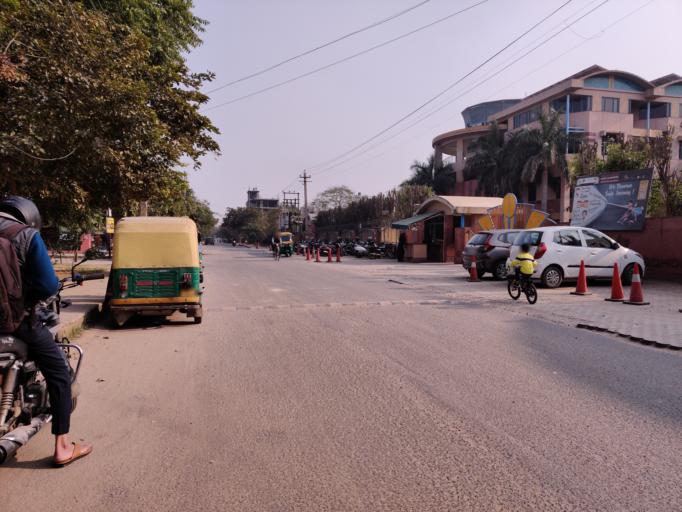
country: IN
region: Haryana
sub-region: Gurgaon
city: Gurgaon
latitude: 28.4425
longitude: 77.0652
